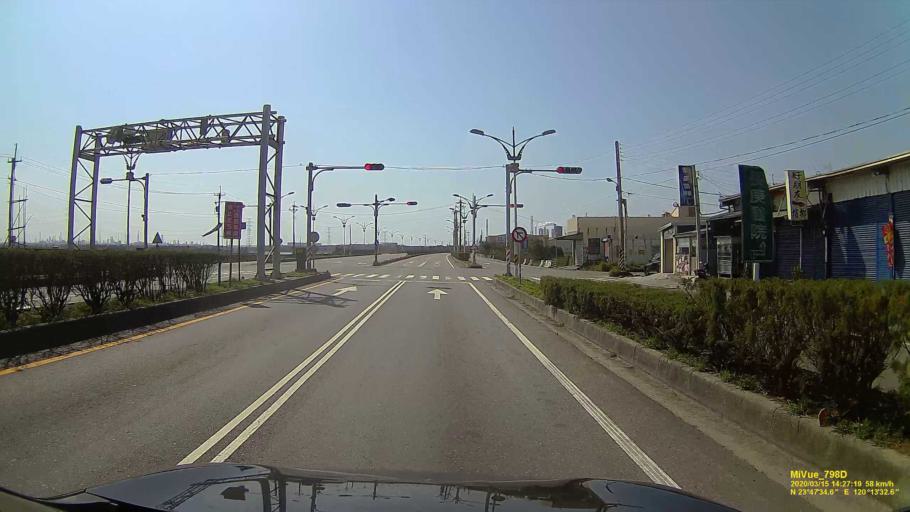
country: TW
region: Taiwan
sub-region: Yunlin
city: Douliu
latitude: 23.7930
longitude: 120.2254
